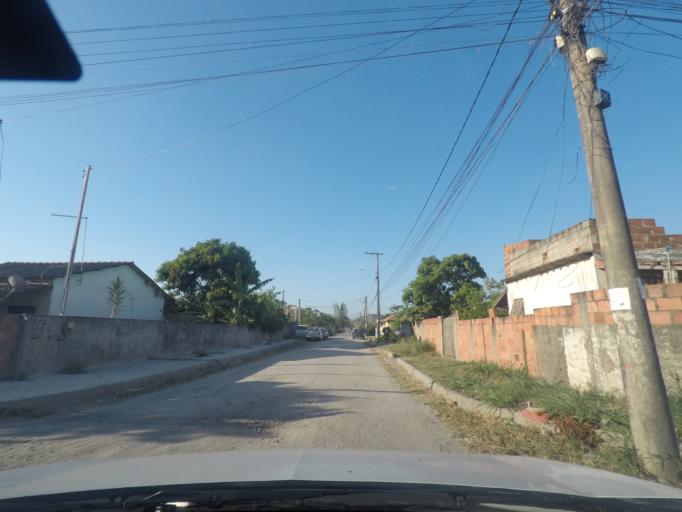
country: BR
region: Rio de Janeiro
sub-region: Marica
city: Marica
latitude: -22.9645
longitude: -42.9370
